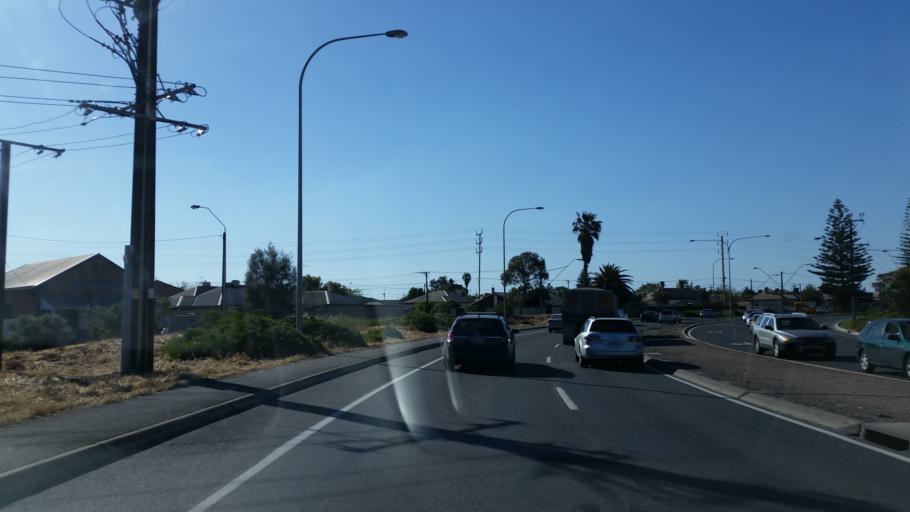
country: AU
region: South Australia
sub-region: Port Adelaide Enfield
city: Birkenhead
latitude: -34.8376
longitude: 138.5023
